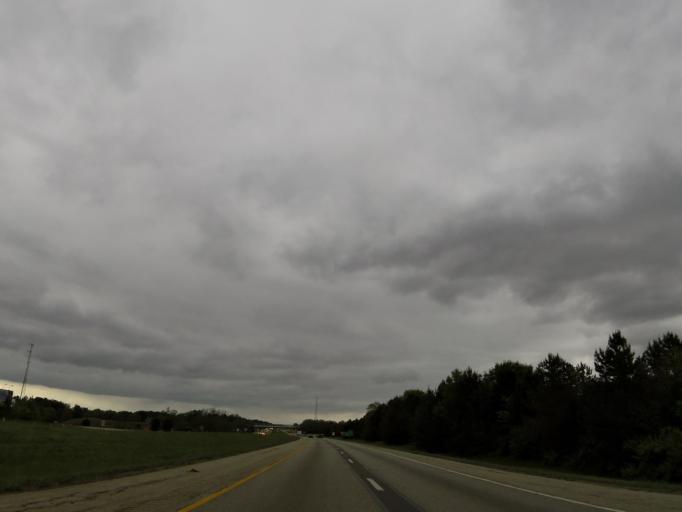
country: US
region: Ohio
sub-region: Warren County
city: Morrow
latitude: 39.4260
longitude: -84.0857
